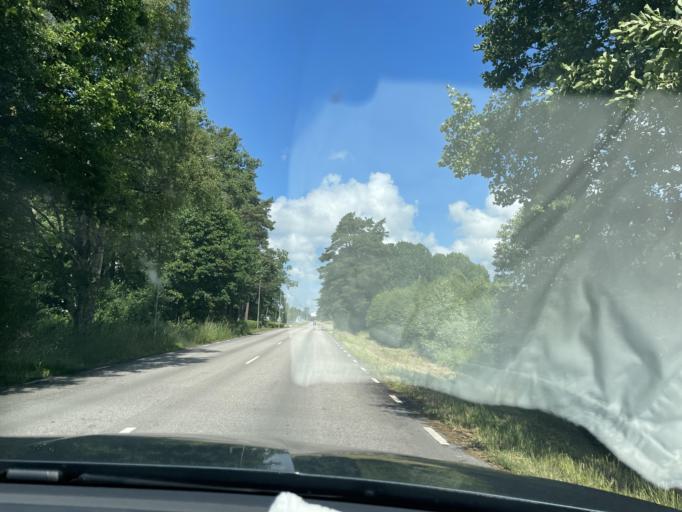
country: SE
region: Kronoberg
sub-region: Vaxjo Kommun
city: Vaexjoe
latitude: 56.8651
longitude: 14.8342
